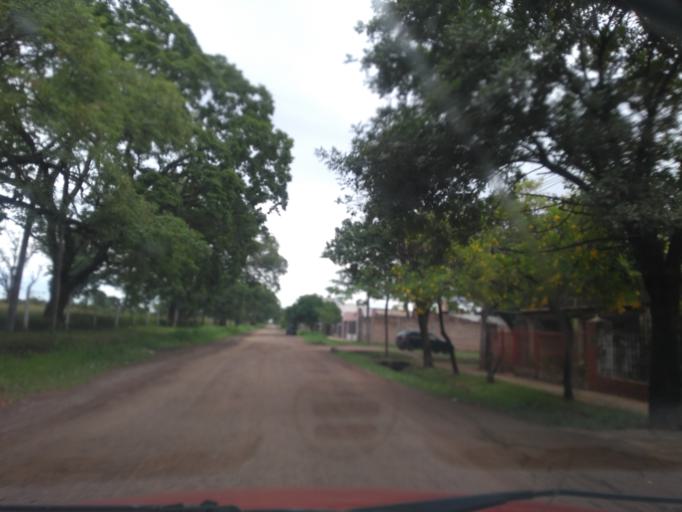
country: AR
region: Chaco
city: Barranqueras
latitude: -27.4787
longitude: -58.9601
